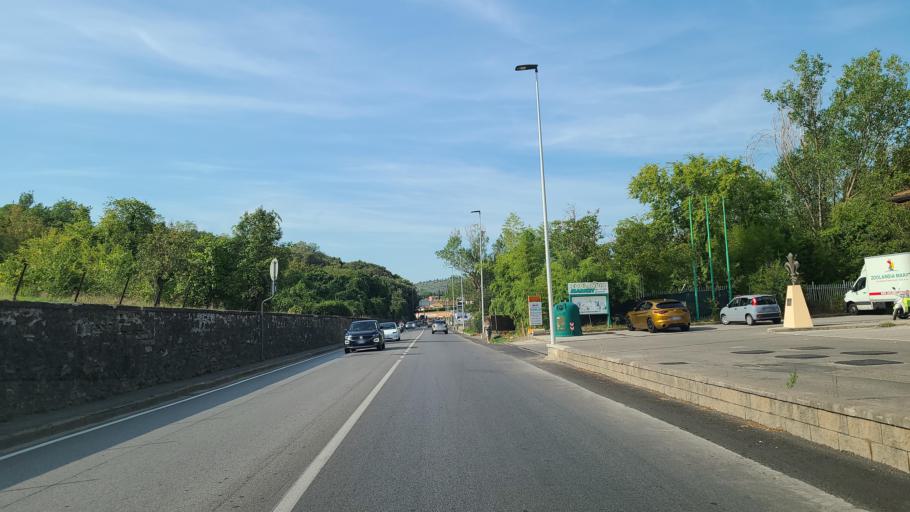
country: IT
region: Tuscany
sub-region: Province of Florence
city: Tavarnuzze
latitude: 43.7441
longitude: 11.2269
